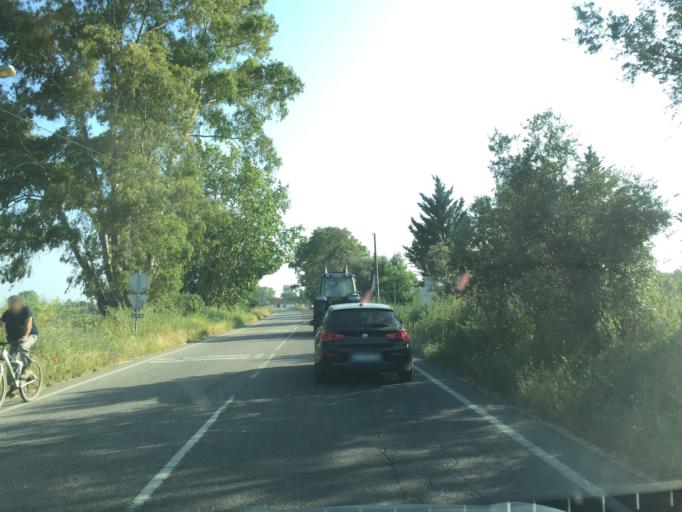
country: PT
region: Santarem
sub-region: Almeirim
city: Almeirim
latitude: 39.2036
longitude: -8.6361
